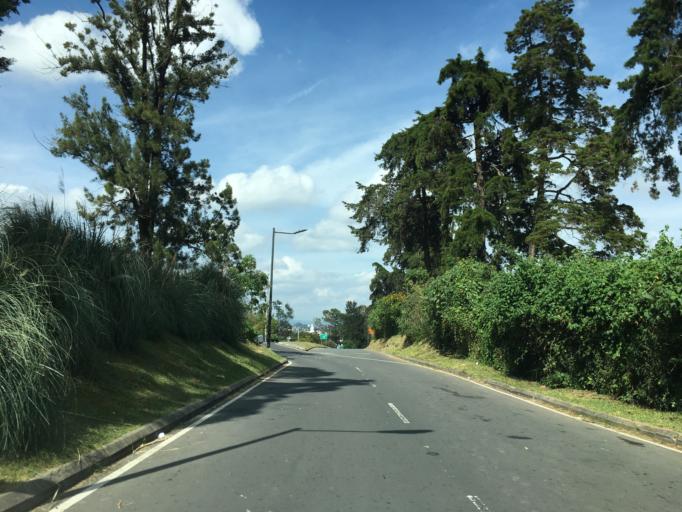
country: GT
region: Guatemala
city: Santa Catarina Pinula
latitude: 14.6045
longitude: -90.4842
